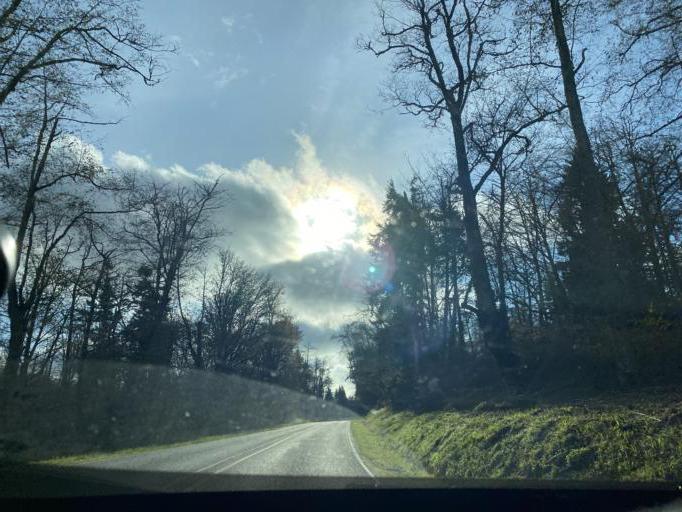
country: US
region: Washington
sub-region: Island County
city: Langley
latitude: 47.9683
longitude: -122.4433
